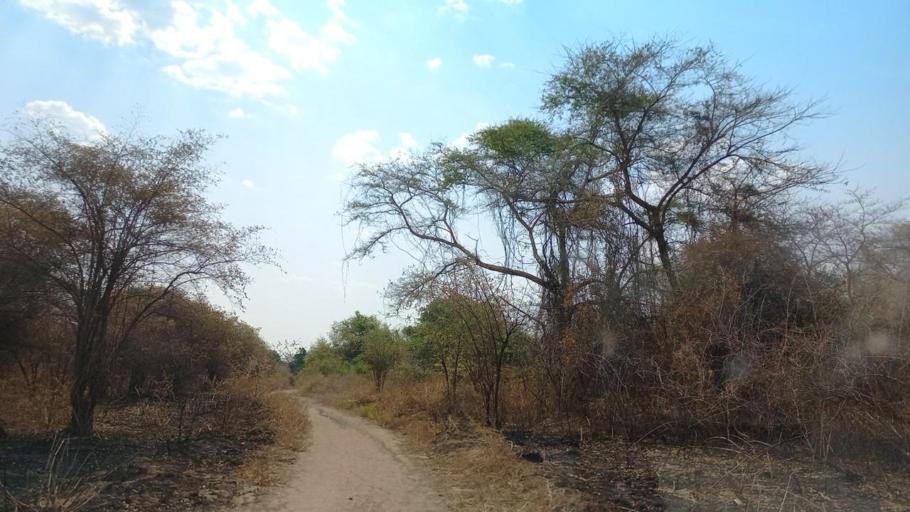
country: ZM
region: Lusaka
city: Luangwa
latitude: -15.0912
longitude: 30.1513
